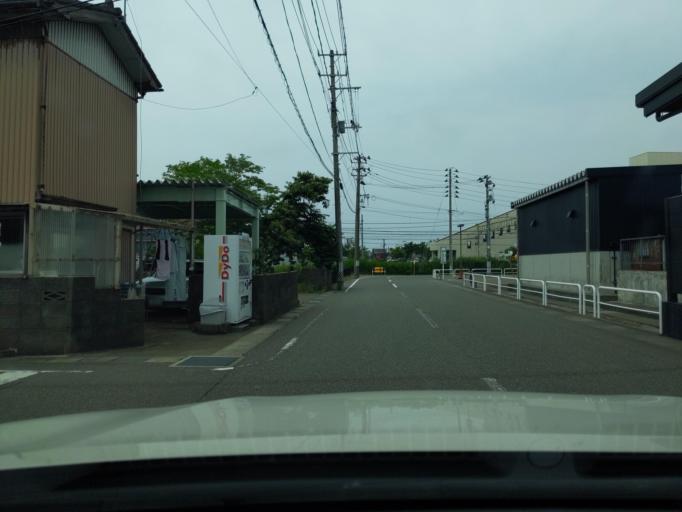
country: JP
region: Niigata
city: Kashiwazaki
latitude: 37.3634
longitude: 138.5612
